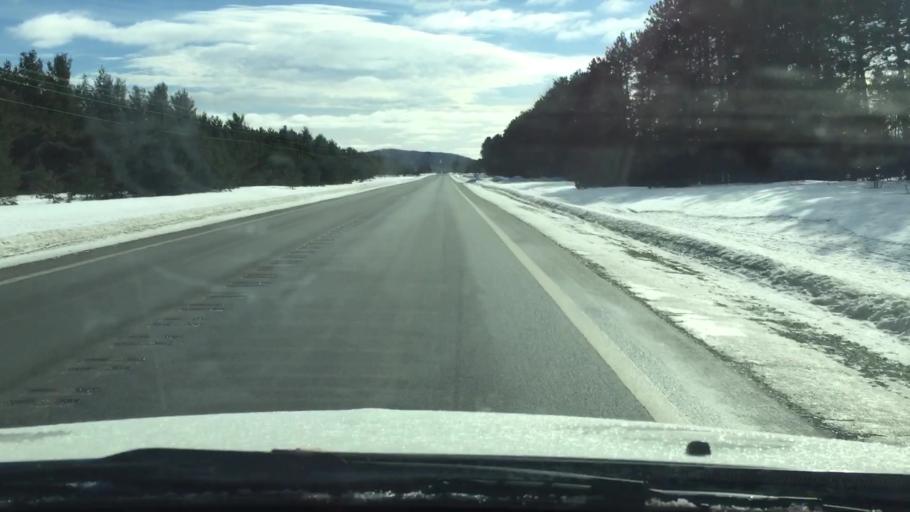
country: US
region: Michigan
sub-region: Antrim County
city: Mancelona
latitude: 44.9253
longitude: -85.0510
